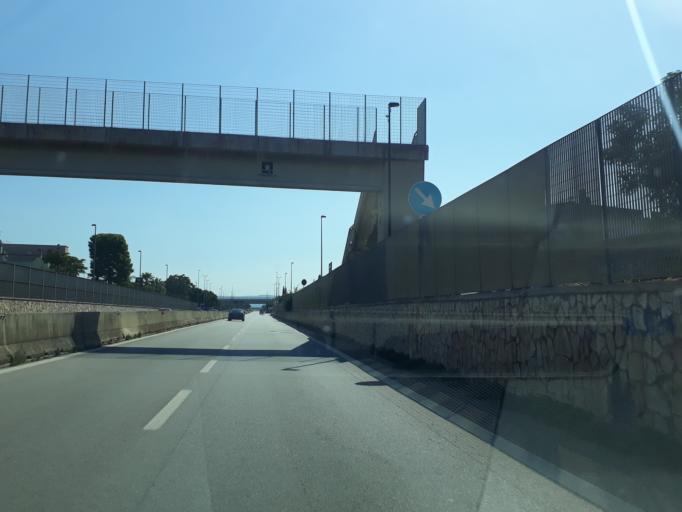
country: IT
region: Apulia
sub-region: Provincia di Brindisi
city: Fasano
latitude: 40.8843
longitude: 17.3361
